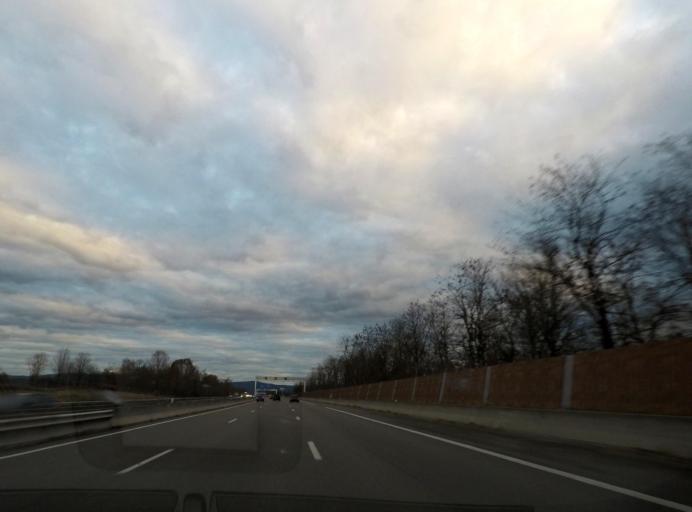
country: FR
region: Rhone-Alpes
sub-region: Departement de l'Ain
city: Saint-Martin-du-Mont
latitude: 46.0779
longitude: 5.2991
